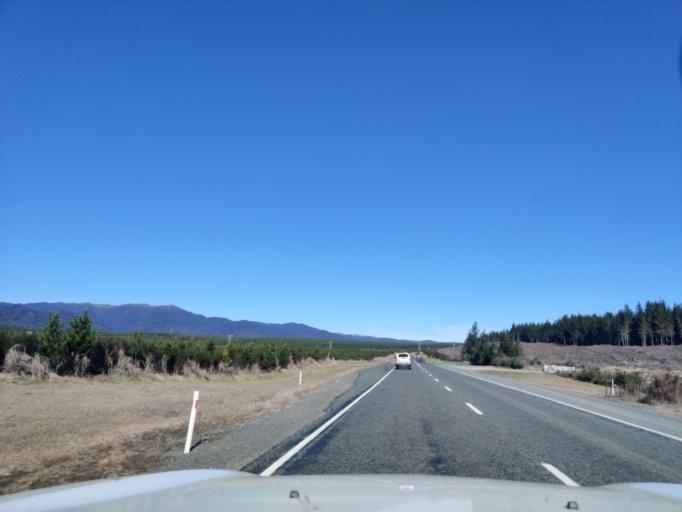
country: NZ
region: Waikato
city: Turangi
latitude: -39.0986
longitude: 175.8089
